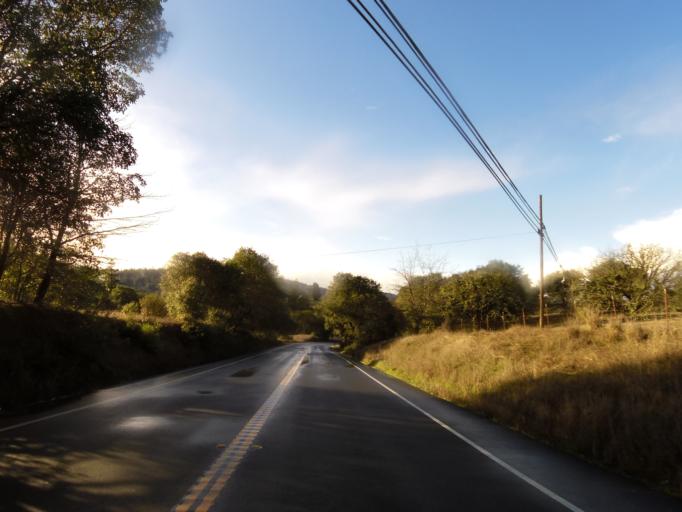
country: US
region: California
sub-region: Mendocino County
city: Boonville
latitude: 39.0550
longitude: -123.4264
